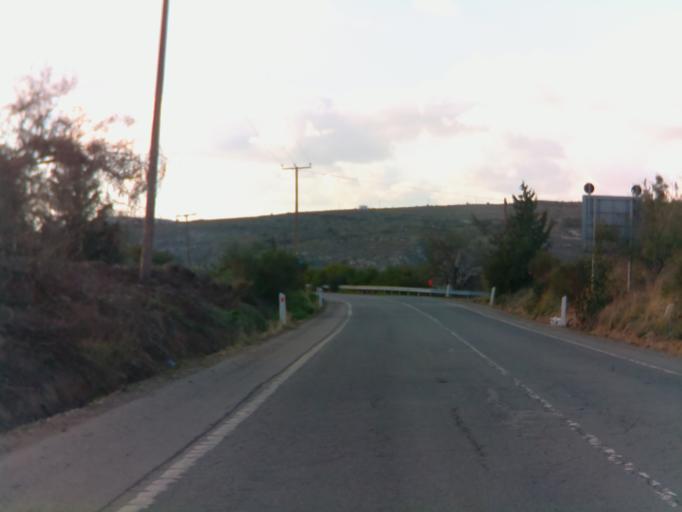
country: CY
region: Pafos
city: Mesogi
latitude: 34.7479
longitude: 32.5095
